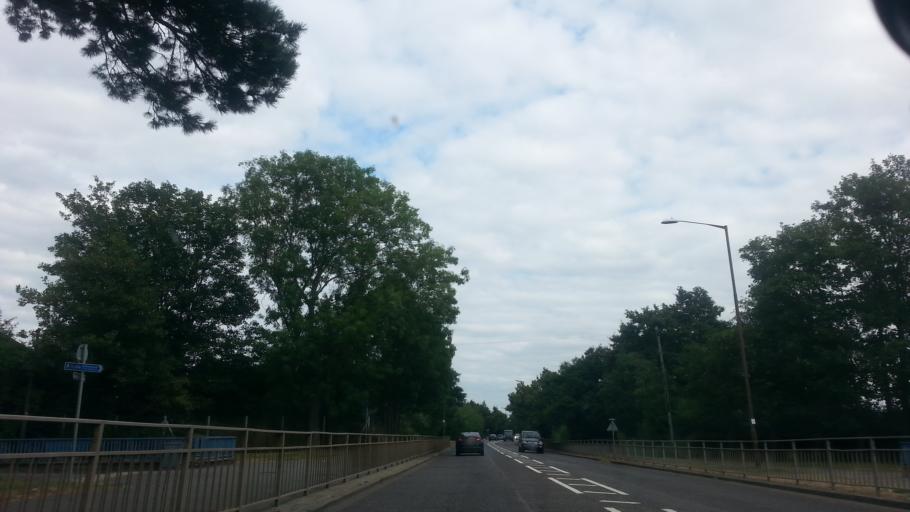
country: GB
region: England
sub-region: Essex
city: Chelmsford
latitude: 51.7216
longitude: 0.4657
